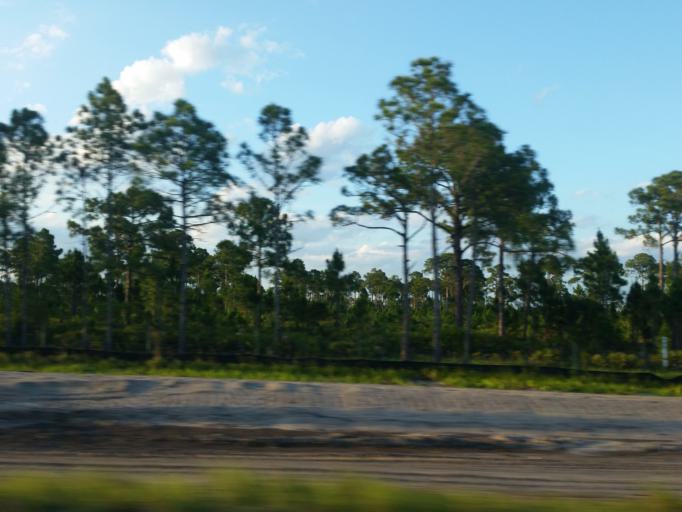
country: US
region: Florida
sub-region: Sarasota County
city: Warm Mineral Springs
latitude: 27.1015
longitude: -82.2850
